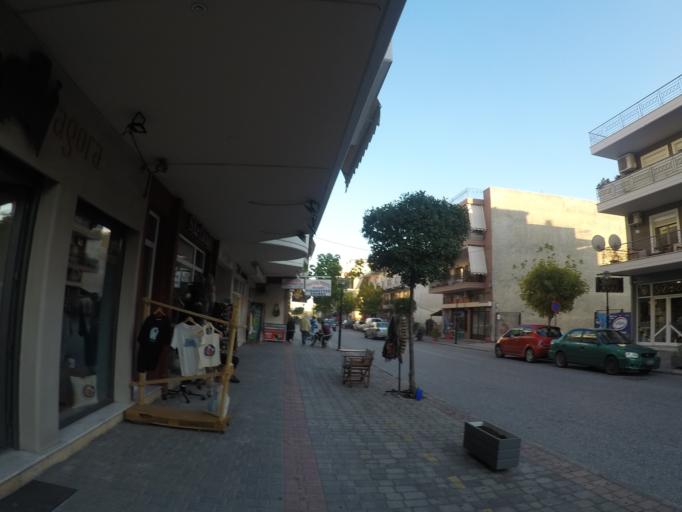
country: GR
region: Thessaly
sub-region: Trikala
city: Kalampaka
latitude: 39.7035
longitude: 21.6305
